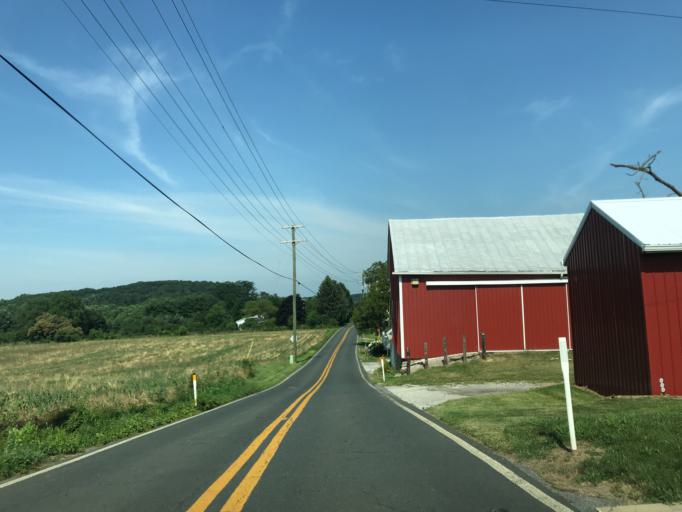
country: US
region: Maryland
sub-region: Carroll County
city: Manchester
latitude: 39.6696
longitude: -76.8693
